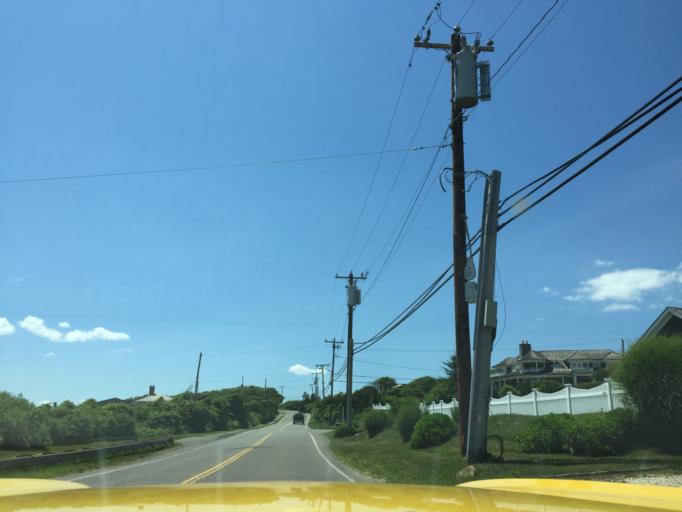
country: US
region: New York
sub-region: Suffolk County
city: Montauk
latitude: 41.0267
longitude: -71.9633
